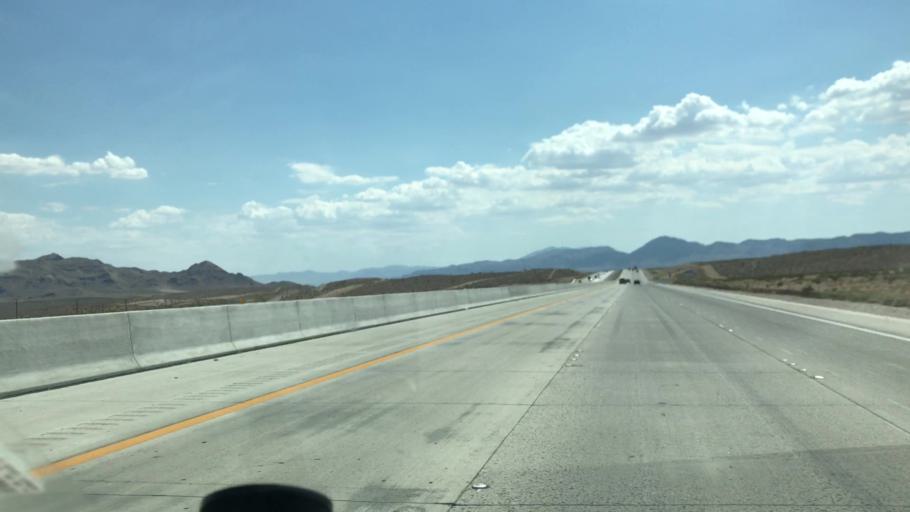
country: US
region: Nevada
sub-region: Clark County
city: Enterprise
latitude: 35.8355
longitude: -115.2838
